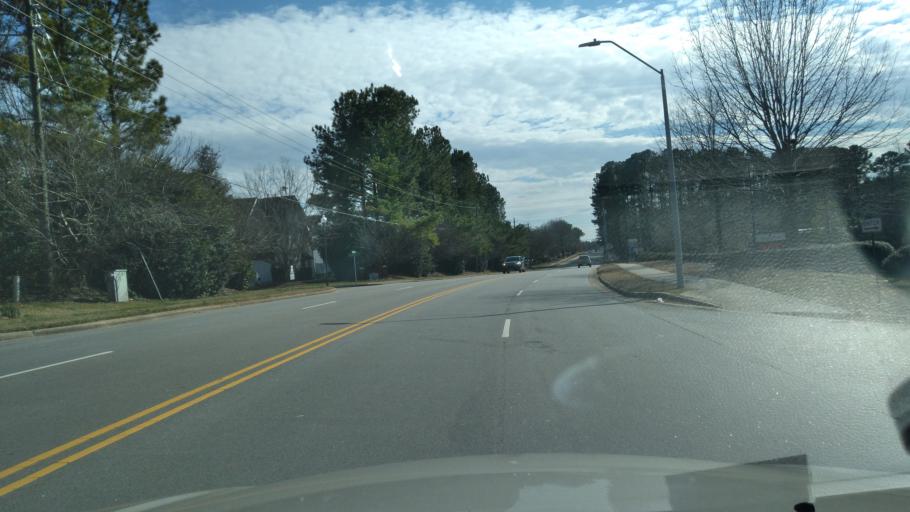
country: US
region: North Carolina
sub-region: Wake County
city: Garner
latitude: 35.6969
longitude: -78.6166
